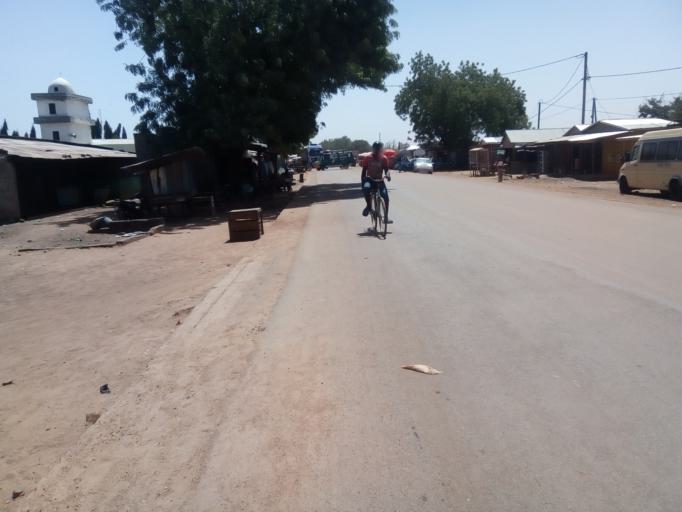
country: GH
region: Upper East
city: Navrongo
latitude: 10.9998
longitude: -1.1152
